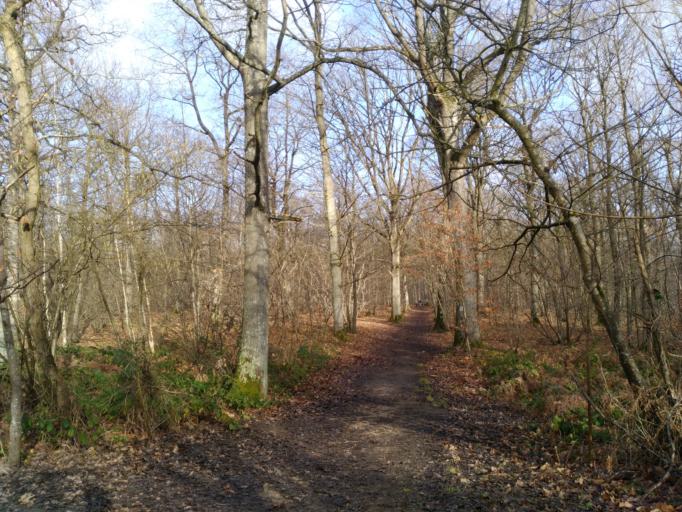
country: FR
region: Ile-de-France
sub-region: Departement des Yvelines
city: Neauphle-le-Chateau
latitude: 48.8016
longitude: 1.9300
